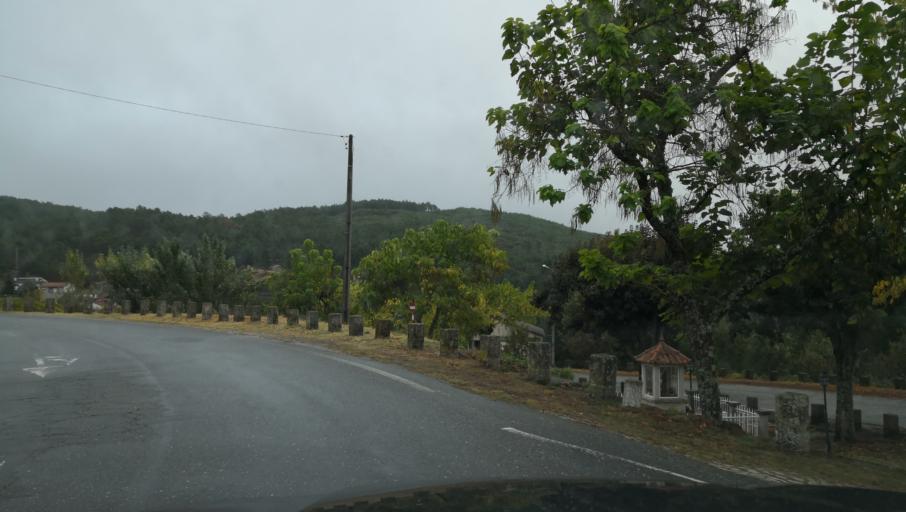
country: PT
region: Vila Real
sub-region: Sabrosa
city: Sabrosa
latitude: 41.3517
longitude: -7.5900
